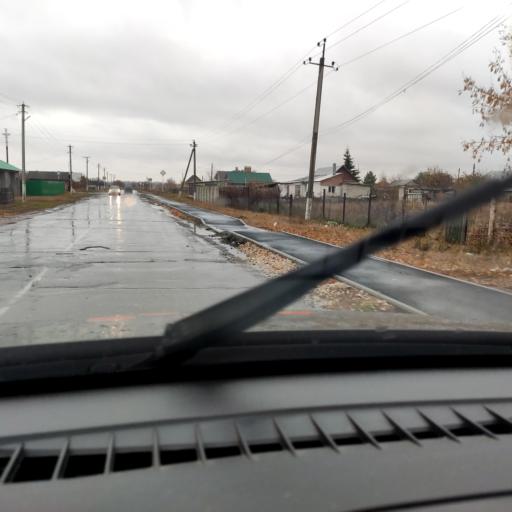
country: RU
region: Samara
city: Khryashchevka
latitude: 53.7318
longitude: 49.1746
